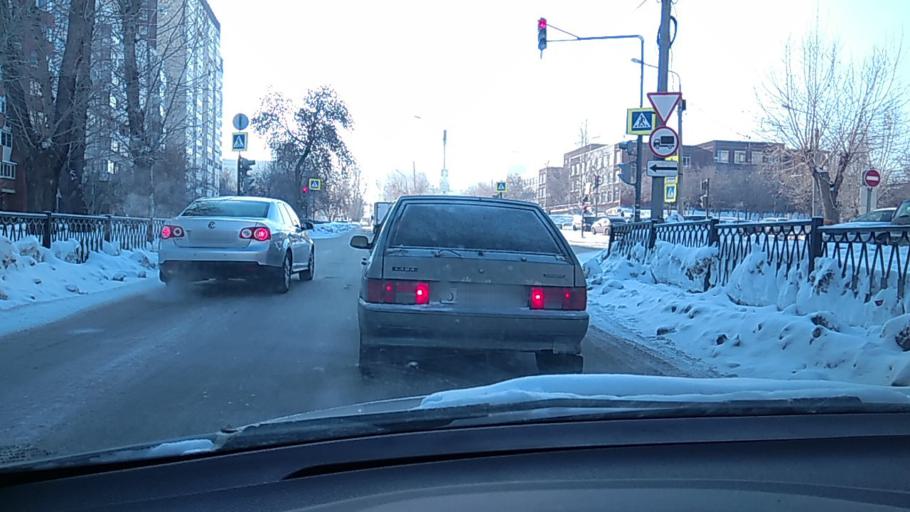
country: RU
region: Sverdlovsk
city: Yekaterinburg
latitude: 56.8127
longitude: 60.5970
